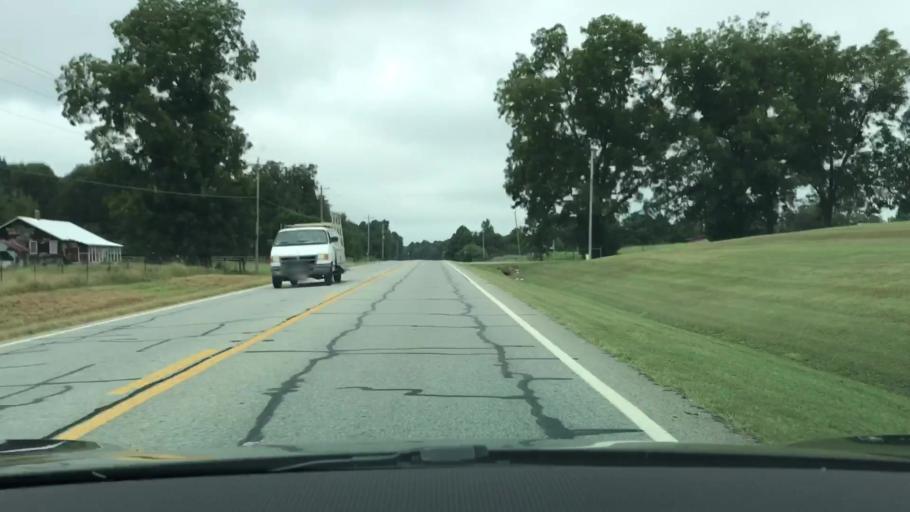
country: US
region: Georgia
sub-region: Oconee County
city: Watkinsville
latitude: 33.8029
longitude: -83.3411
